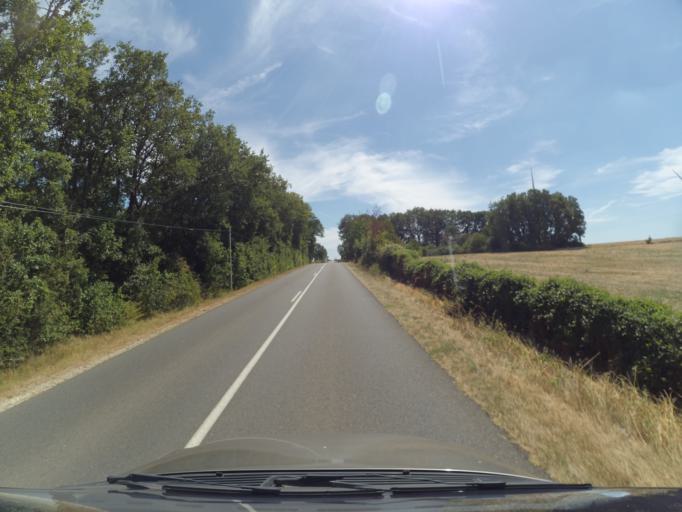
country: FR
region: Poitou-Charentes
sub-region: Departement de la Vienne
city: Usson-du-Poitou
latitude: 46.2358
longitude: 0.5271
